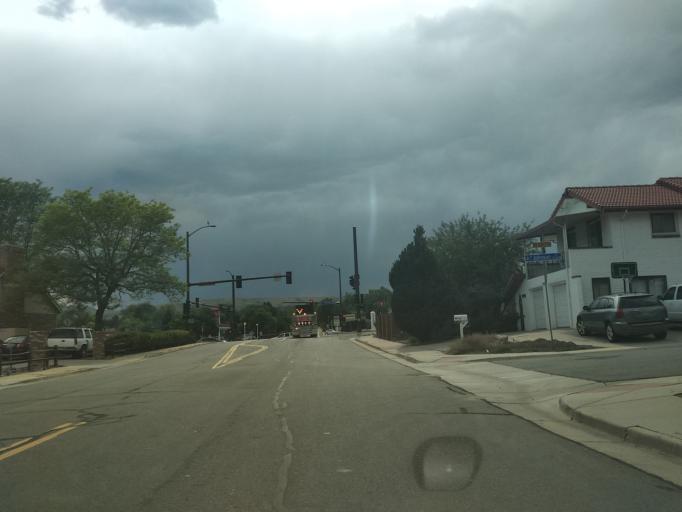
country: US
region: Colorado
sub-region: Jefferson County
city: Lakewood
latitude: 39.7004
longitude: -105.1085
